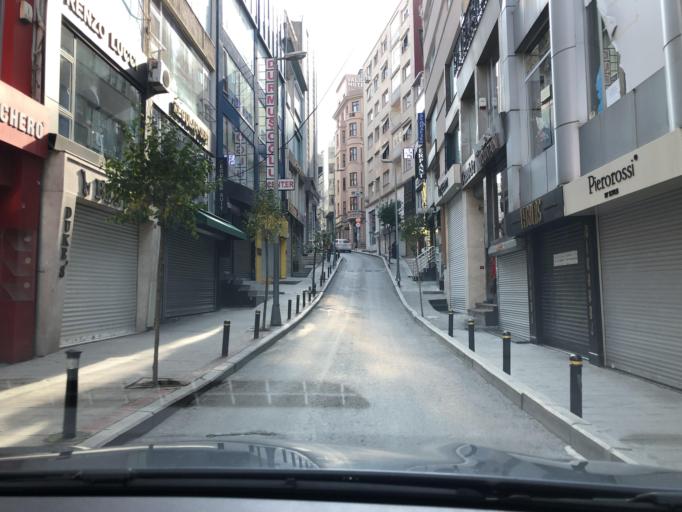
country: TR
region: Istanbul
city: Sisli
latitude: 41.0563
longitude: 28.9883
